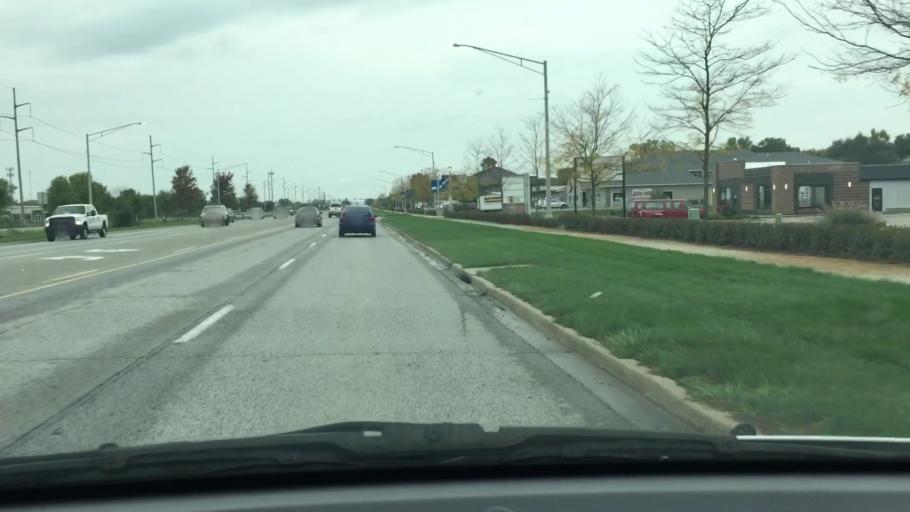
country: US
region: Iowa
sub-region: Johnson County
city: Coralville
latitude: 41.6766
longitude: -91.5858
